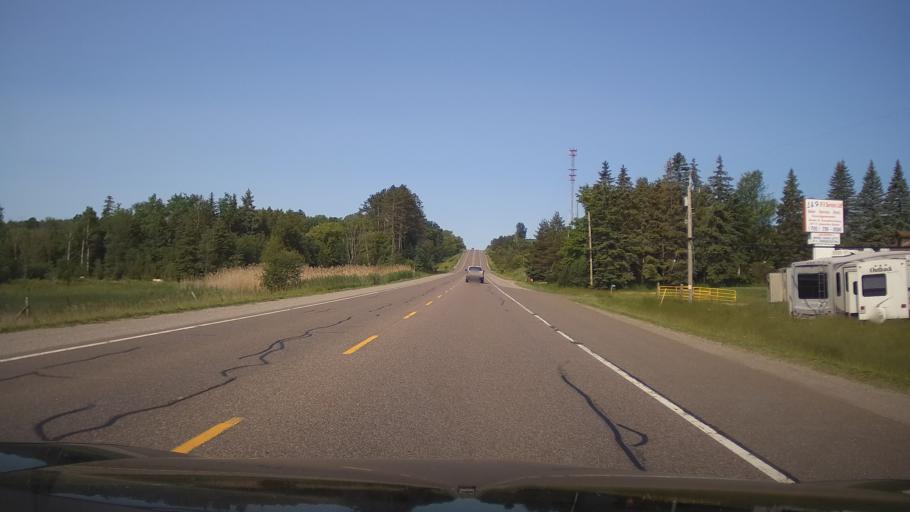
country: CA
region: Ontario
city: Omemee
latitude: 44.3183
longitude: -78.4804
